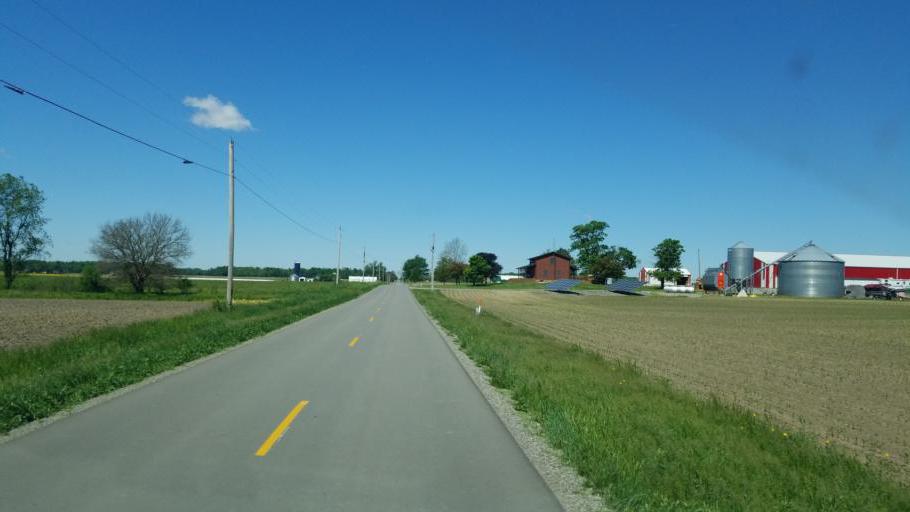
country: US
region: Ohio
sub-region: Shelby County
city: Jackson Center
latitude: 40.4174
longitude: -83.9794
